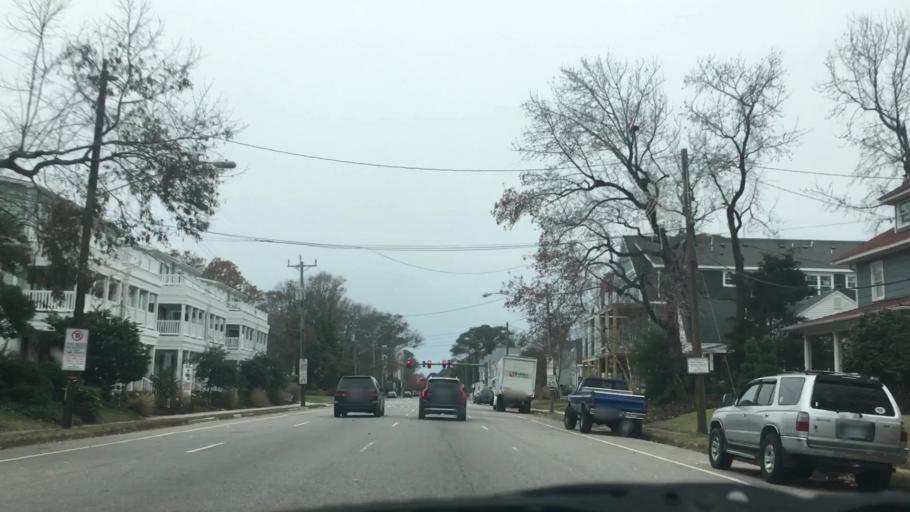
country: US
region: Virginia
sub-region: City of Virginia Beach
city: Virginia Beach
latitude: 36.8497
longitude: -75.9788
